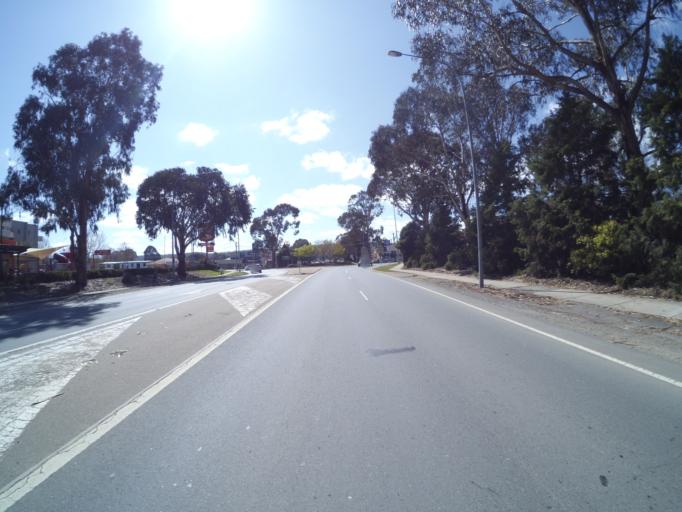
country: AU
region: New South Wales
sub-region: Queanbeyan
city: Queanbeyan
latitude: -35.3506
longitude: 149.2403
